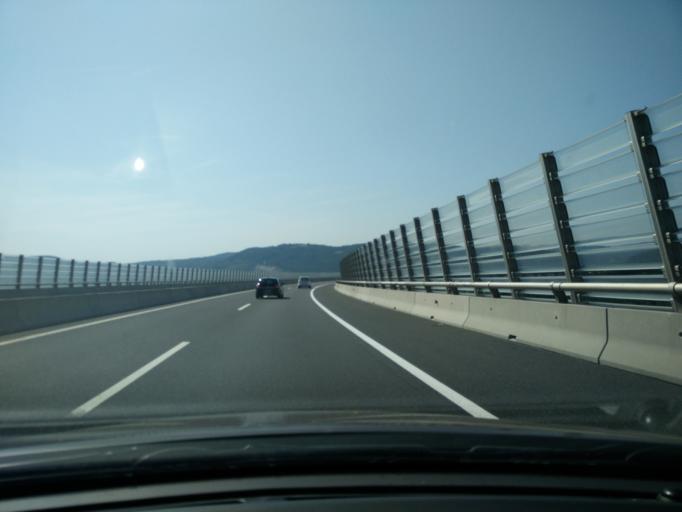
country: IT
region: Friuli Venezia Giulia
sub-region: Provincia di Trieste
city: Dolina
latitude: 45.5584
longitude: 13.8714
